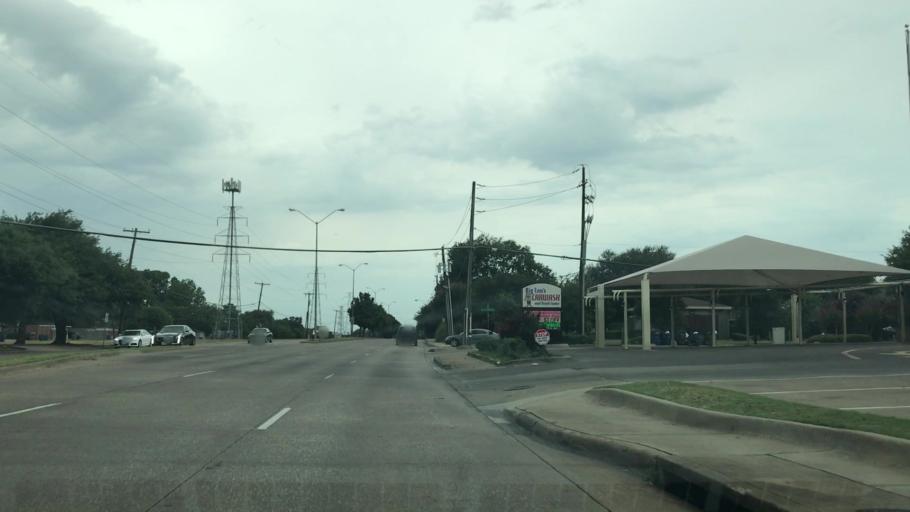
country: US
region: Texas
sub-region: Dallas County
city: Richardson
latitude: 32.9508
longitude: -96.7708
